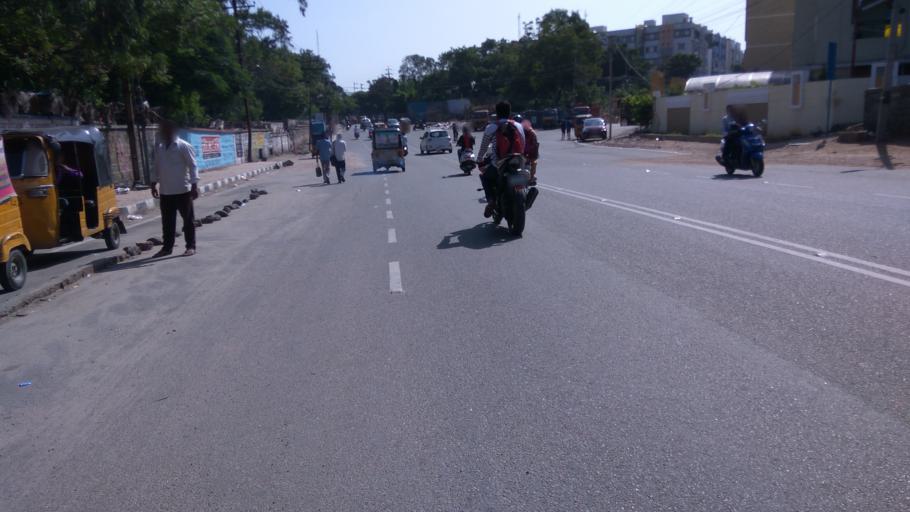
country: IN
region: Telangana
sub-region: Rangareddi
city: Kukatpalli
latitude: 17.4565
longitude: 78.4348
